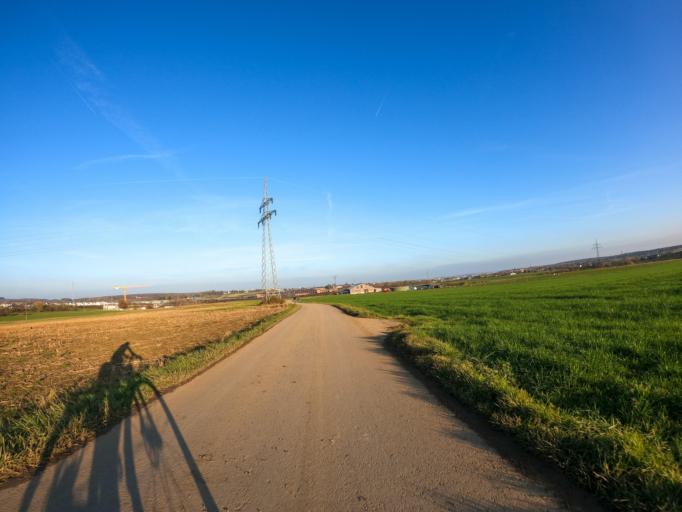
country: LU
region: Luxembourg
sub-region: Canton de Capellen
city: Mamer
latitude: 49.6149
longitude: 6.0236
